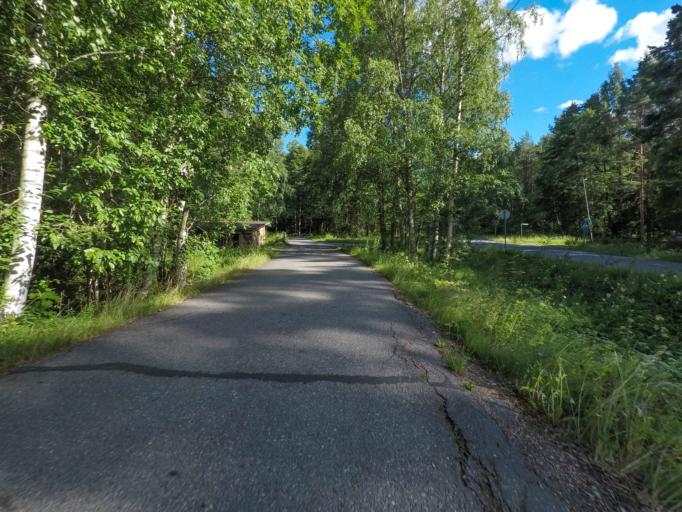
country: FI
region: South Karelia
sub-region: Lappeenranta
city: Lappeenranta
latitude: 61.0865
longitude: 28.1453
